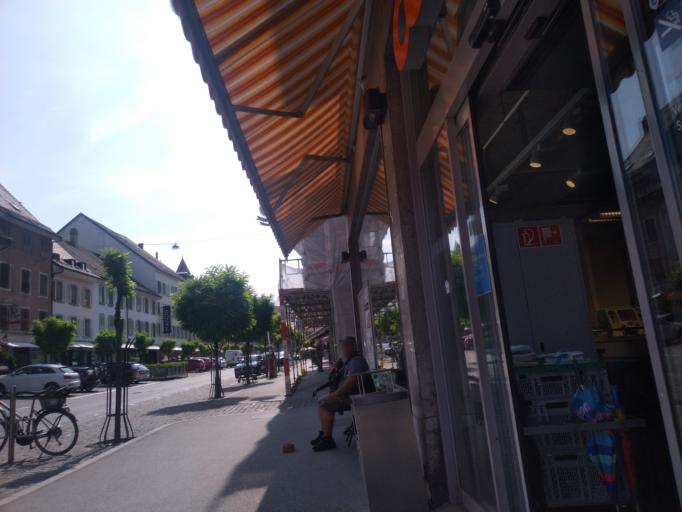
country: CH
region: Fribourg
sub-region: Gruyere District
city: Bulle
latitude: 46.6193
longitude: 7.0576
